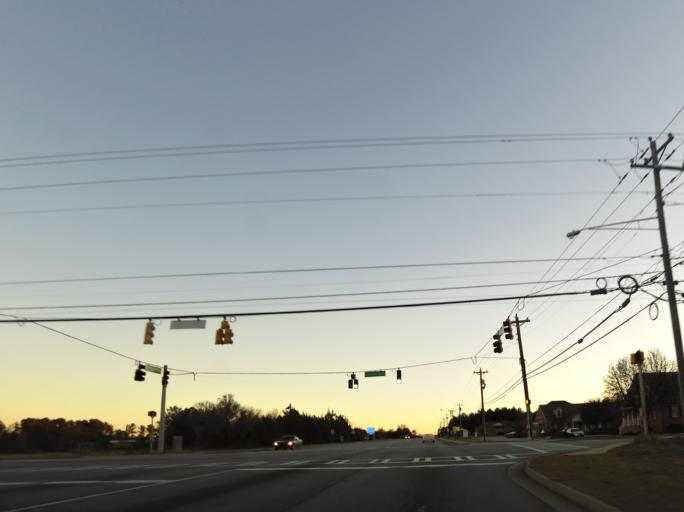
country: US
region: Georgia
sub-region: Houston County
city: Centerville
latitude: 32.6023
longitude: -83.6652
